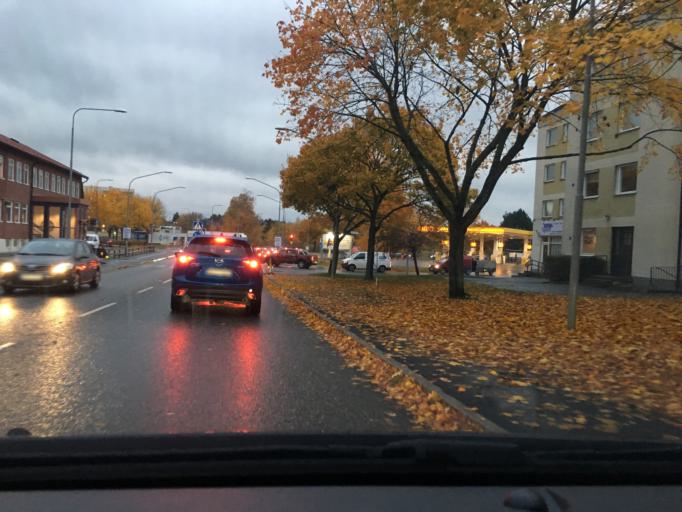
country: SE
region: Stockholm
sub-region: Stockholms Kommun
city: Kista
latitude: 59.3778
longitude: 17.9039
